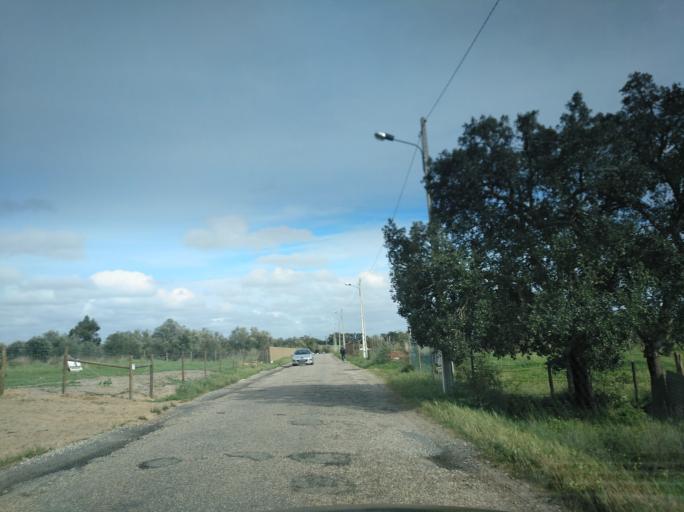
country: PT
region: Setubal
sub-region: Grandola
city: Grandola
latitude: 38.1877
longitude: -8.5594
